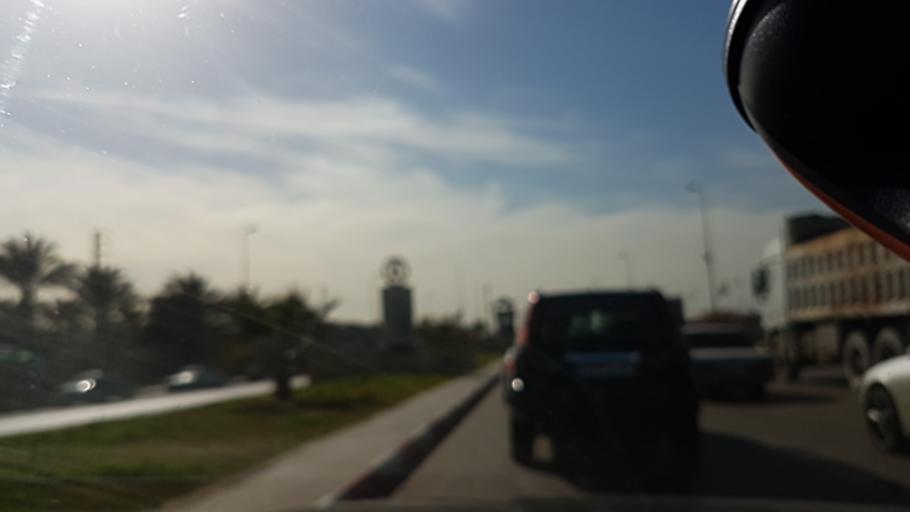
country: LB
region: Liban-Sud
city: Sidon
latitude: 33.5921
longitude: 35.3879
